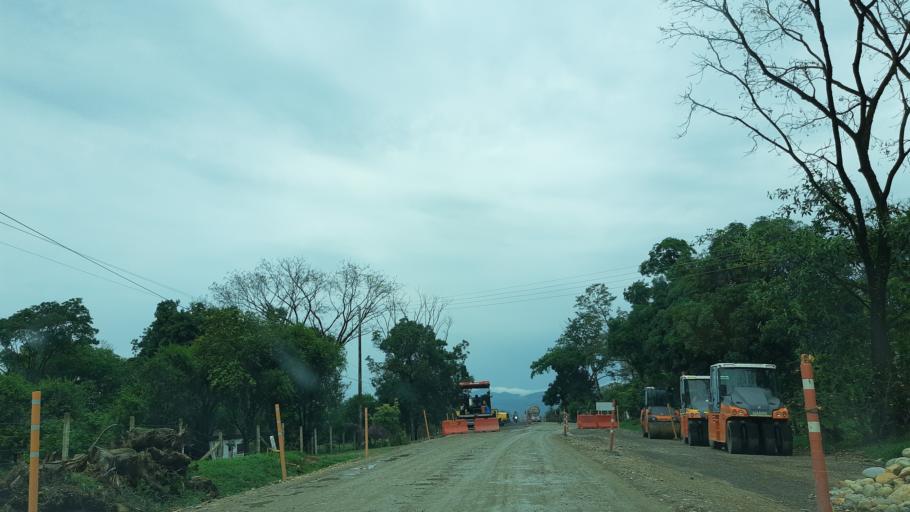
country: CO
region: Casanare
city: Monterrey
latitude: 4.8313
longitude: -72.9600
